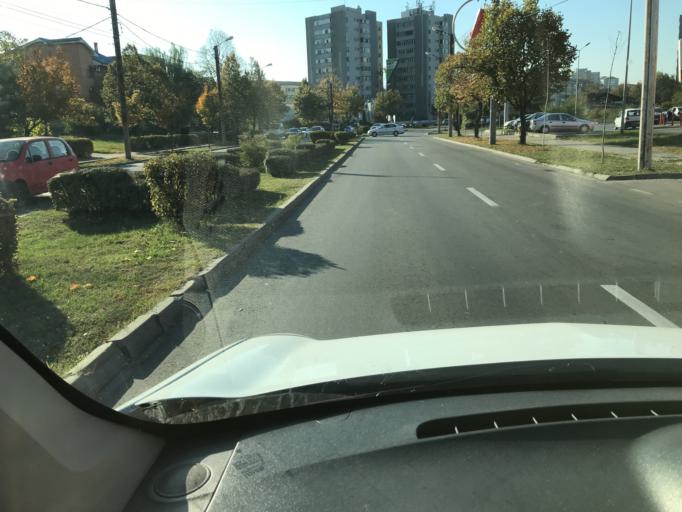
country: RO
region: Olt
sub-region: Municipiul Slatina
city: Slatina
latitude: 44.4376
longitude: 24.3710
